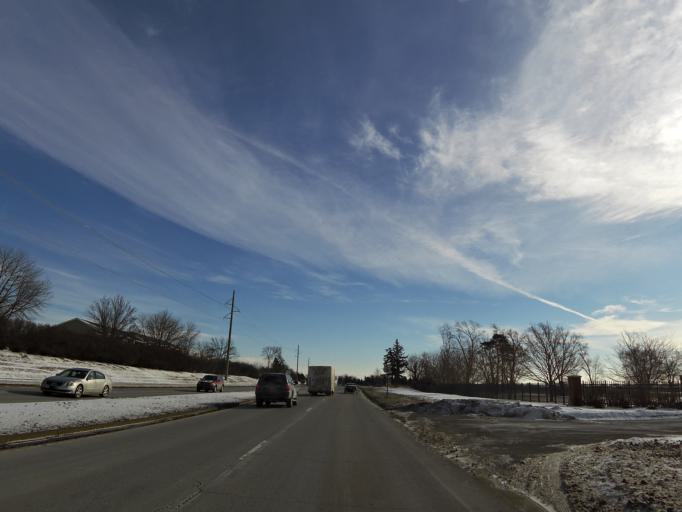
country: US
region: Minnesota
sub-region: Dakota County
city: Apple Valley
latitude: 44.7319
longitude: -93.1753
